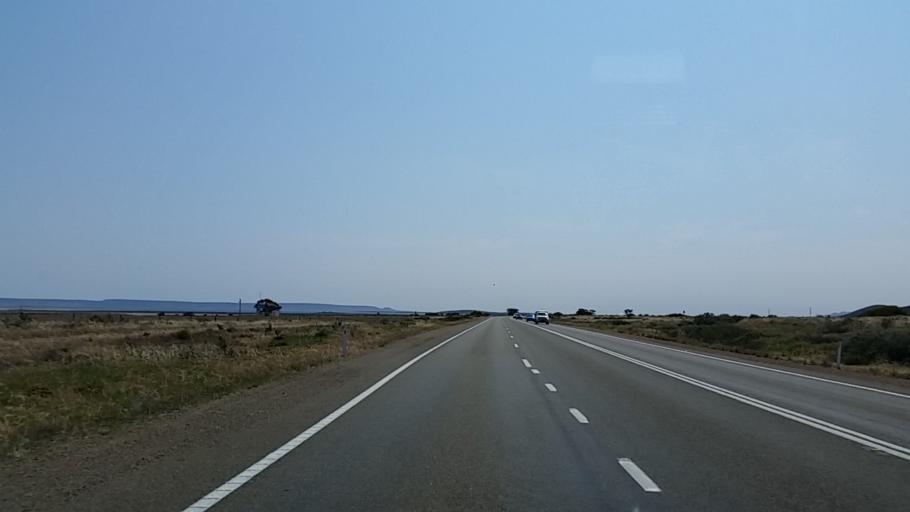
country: AU
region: South Australia
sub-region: Port Augusta
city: Port Augusta
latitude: -32.8083
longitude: 137.9658
